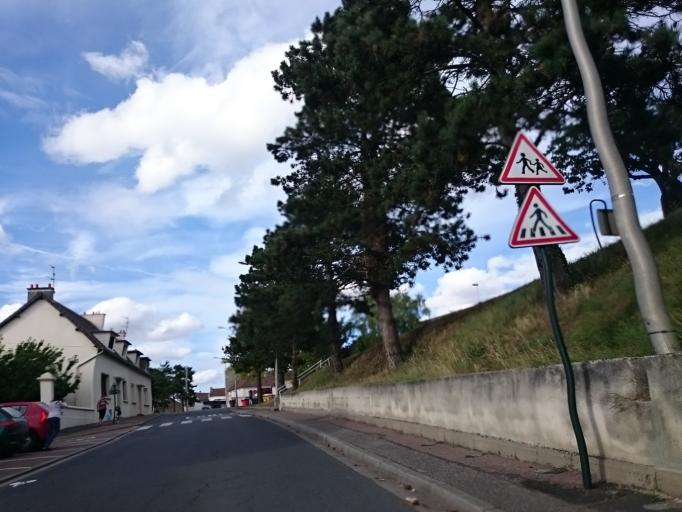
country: FR
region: Lower Normandy
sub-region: Departement du Calvados
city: Fleury-sur-Orne
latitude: 49.1477
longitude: -0.3768
